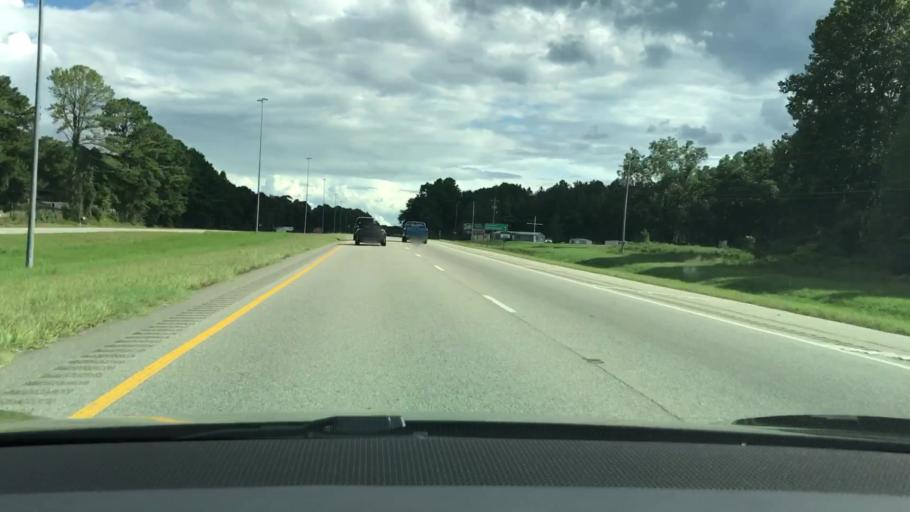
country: US
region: Alabama
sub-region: Pike County
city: Troy
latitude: 31.8406
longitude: -85.9938
